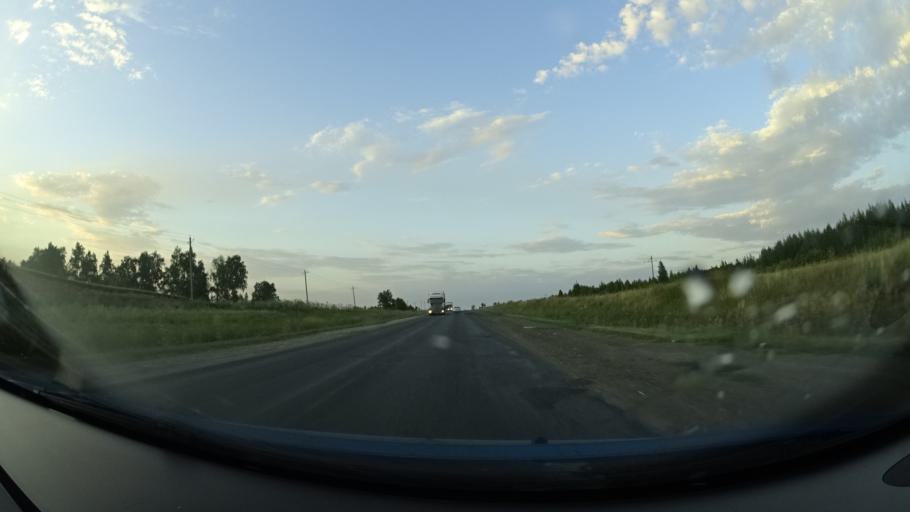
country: RU
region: Orenburg
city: Severnoye
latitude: 54.1851
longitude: 52.6654
